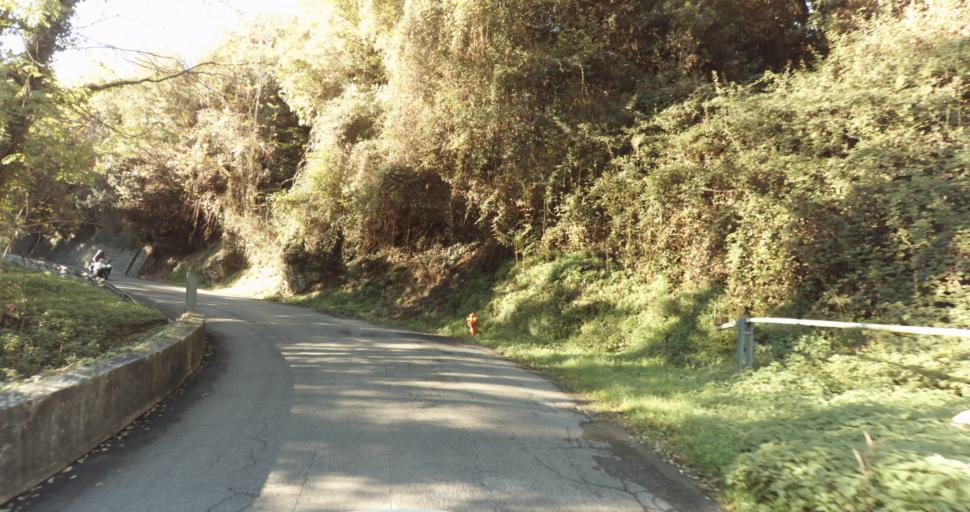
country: FR
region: Provence-Alpes-Cote d'Azur
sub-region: Departement des Alpes-Maritimes
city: Vence
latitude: 43.7277
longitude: 7.0869
